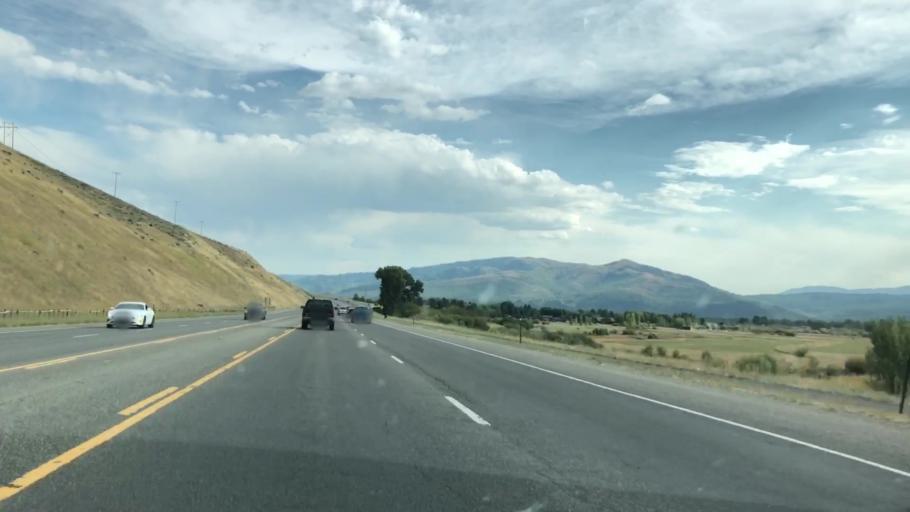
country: US
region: Wyoming
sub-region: Teton County
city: Rafter J Ranch
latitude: 43.4430
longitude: -110.7887
